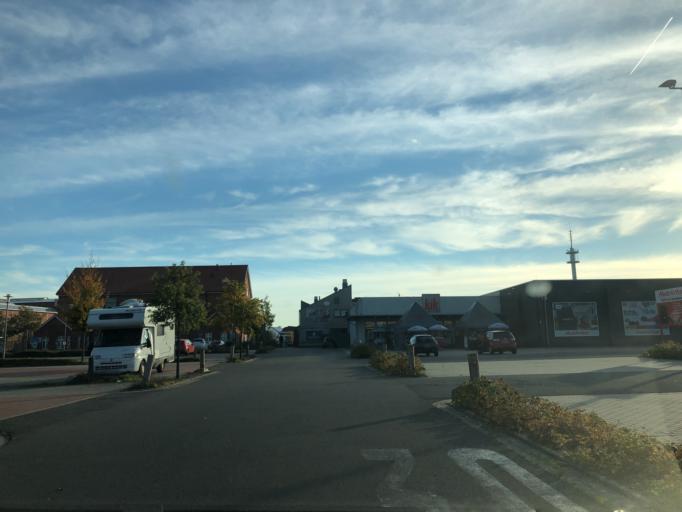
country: DE
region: Lower Saxony
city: Papenburg
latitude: 53.0858
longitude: 7.3840
